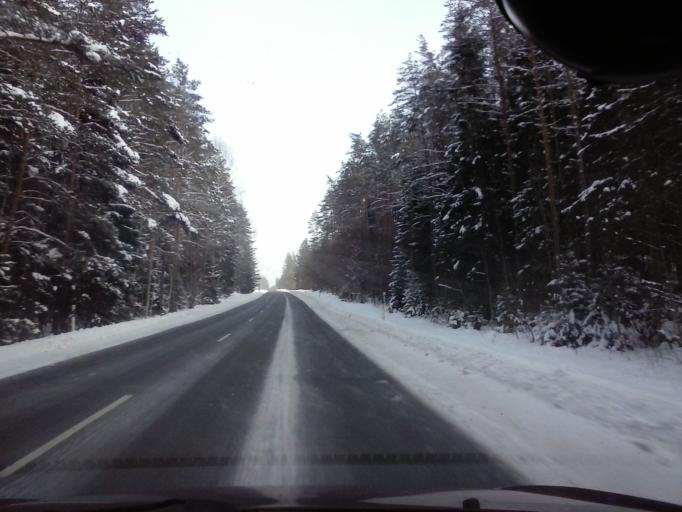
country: EE
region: Viljandimaa
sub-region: Moisakuela linn
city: Moisakula
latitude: 58.2477
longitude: 25.1620
